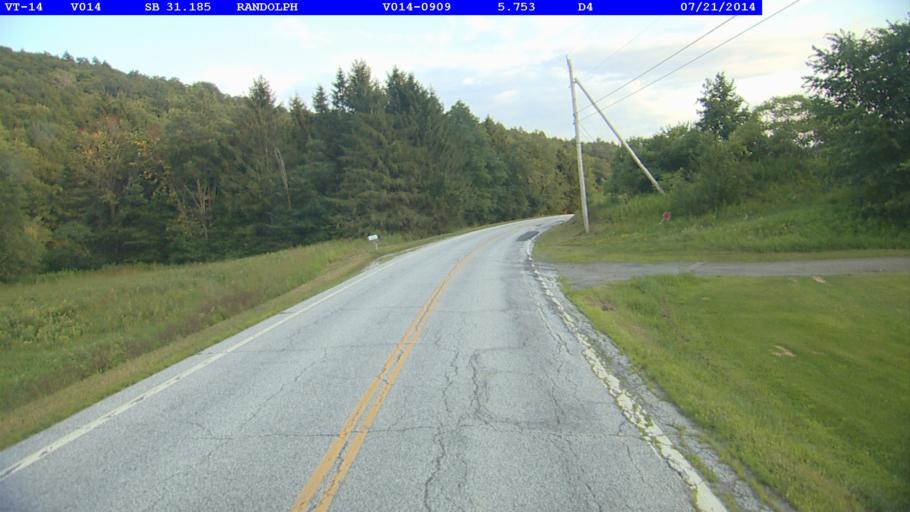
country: US
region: Vermont
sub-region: Orange County
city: Chelsea
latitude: 43.9513
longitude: -72.5501
